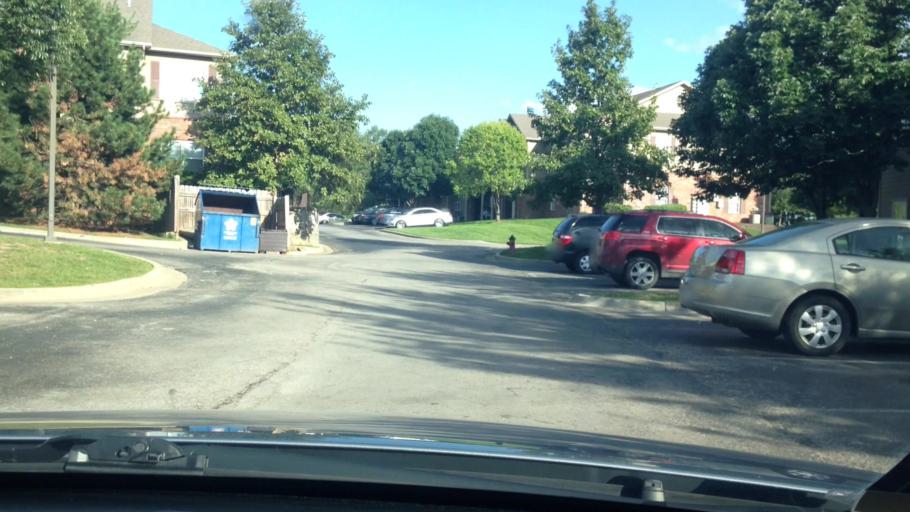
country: US
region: Missouri
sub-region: Clay County
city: Claycomo
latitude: 39.1723
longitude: -94.5055
